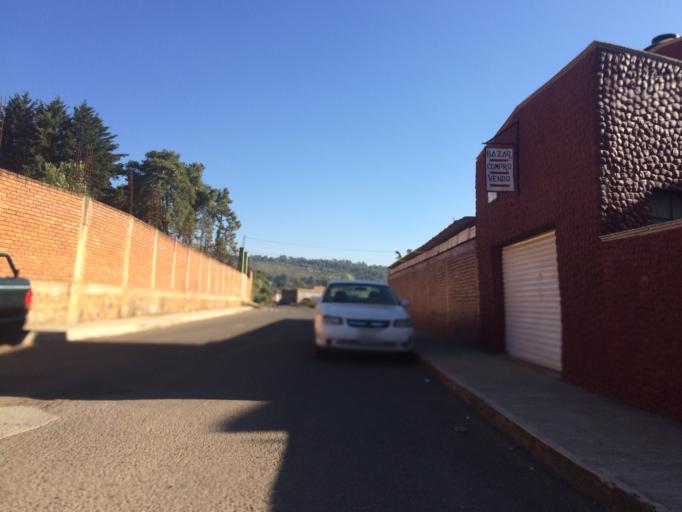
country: MX
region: Michoacan
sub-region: Patzcuaro
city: Colonia Vista Bella (Lomas del Peaje)
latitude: 19.5032
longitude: -101.5998
